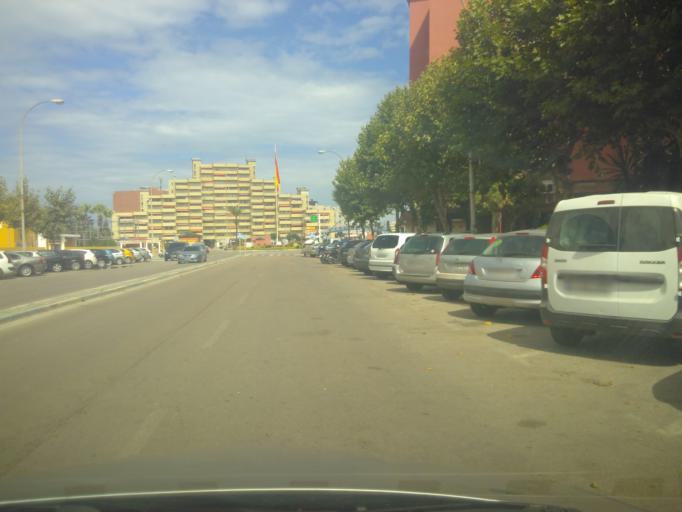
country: ES
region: Andalusia
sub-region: Provincia de Cadiz
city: La Linea de la Concepcion
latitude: 36.1594
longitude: -5.3502
